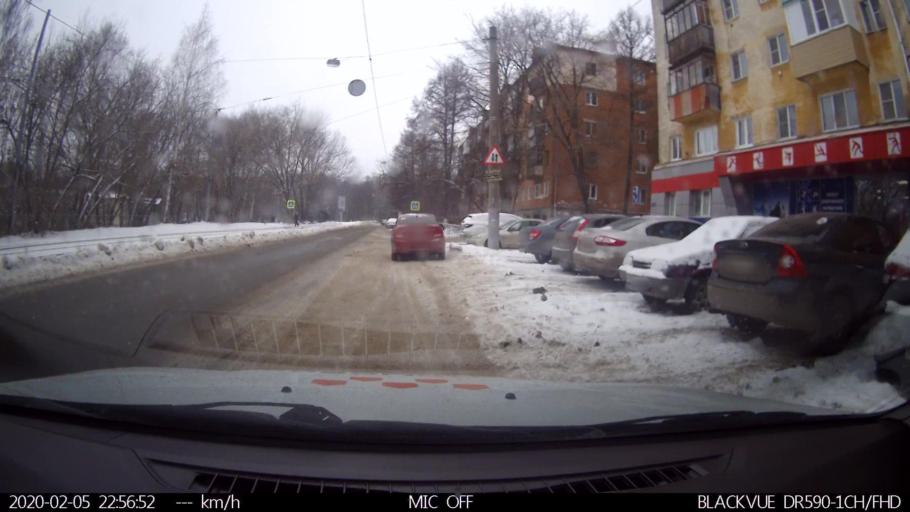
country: RU
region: Penza
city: Bogoslovka
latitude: 53.2826
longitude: 44.8334
